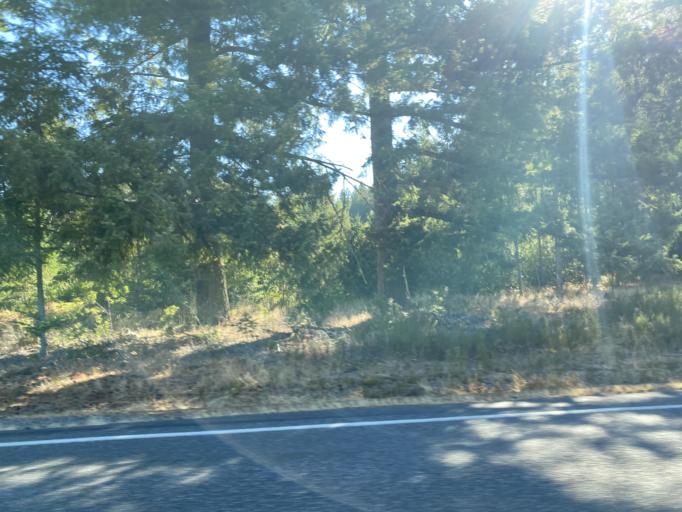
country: US
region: Washington
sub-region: Thurston County
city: Rainier
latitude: 46.9503
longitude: -122.7654
